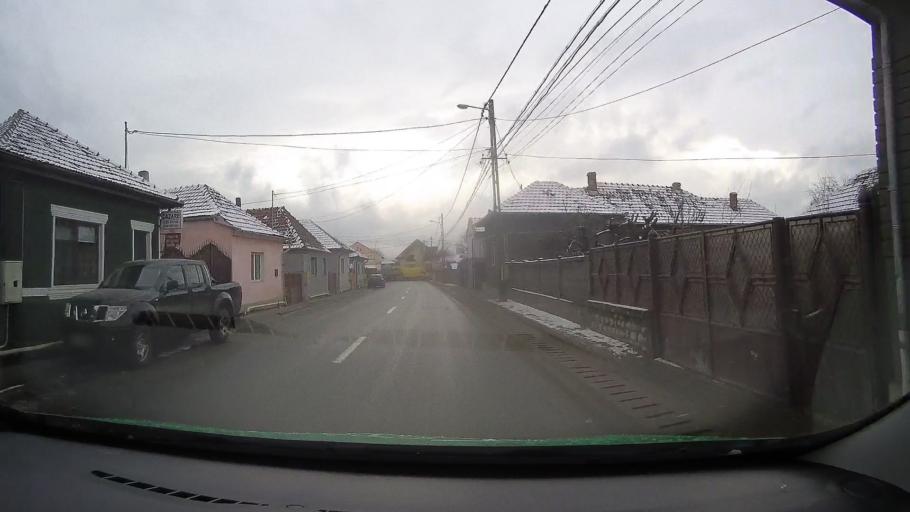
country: RO
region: Hunedoara
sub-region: Oras Hateg
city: Hateg
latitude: 45.6139
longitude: 22.9448
